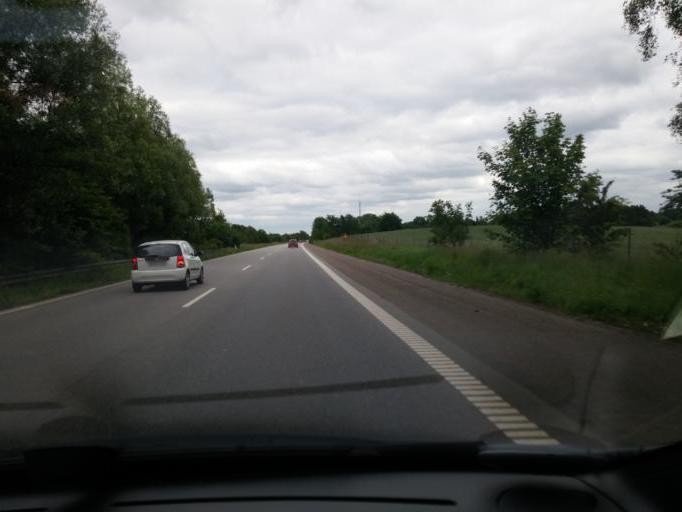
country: DK
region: Capital Region
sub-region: Fureso Kommune
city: Farum
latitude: 55.8337
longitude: 12.3646
